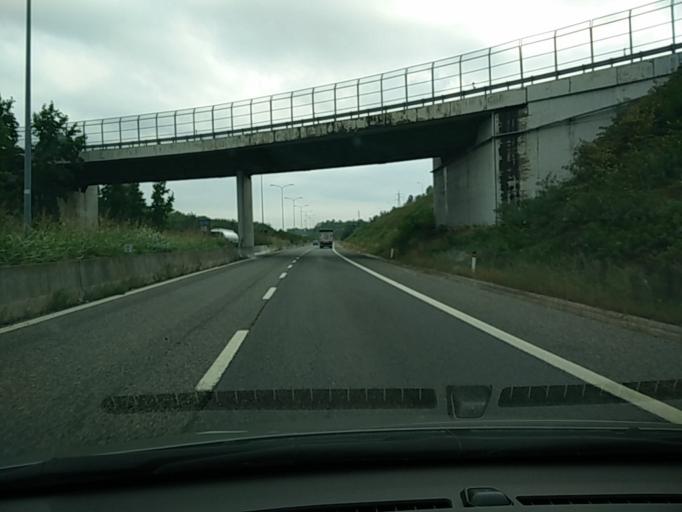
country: IT
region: Lombardy
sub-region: Provincia di Varese
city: Vizzola Ticino
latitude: 45.6257
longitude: 8.7058
